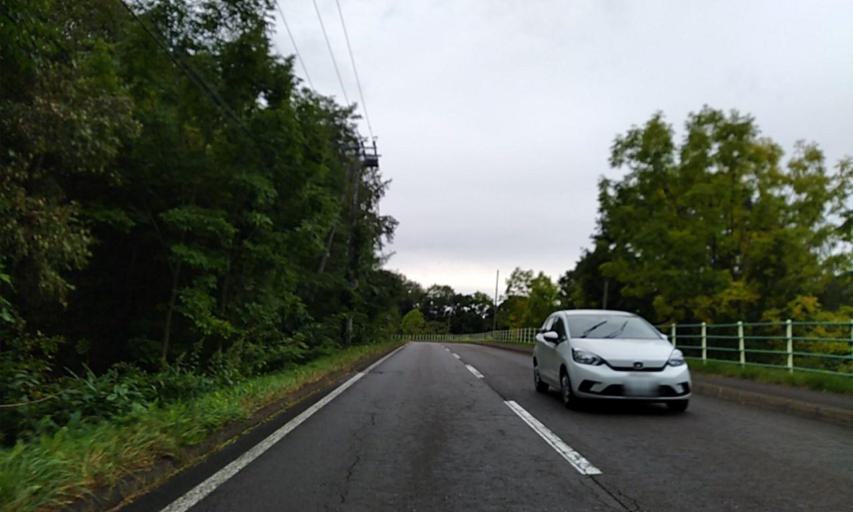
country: JP
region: Hokkaido
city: Abashiri
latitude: 43.9994
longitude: 144.2291
